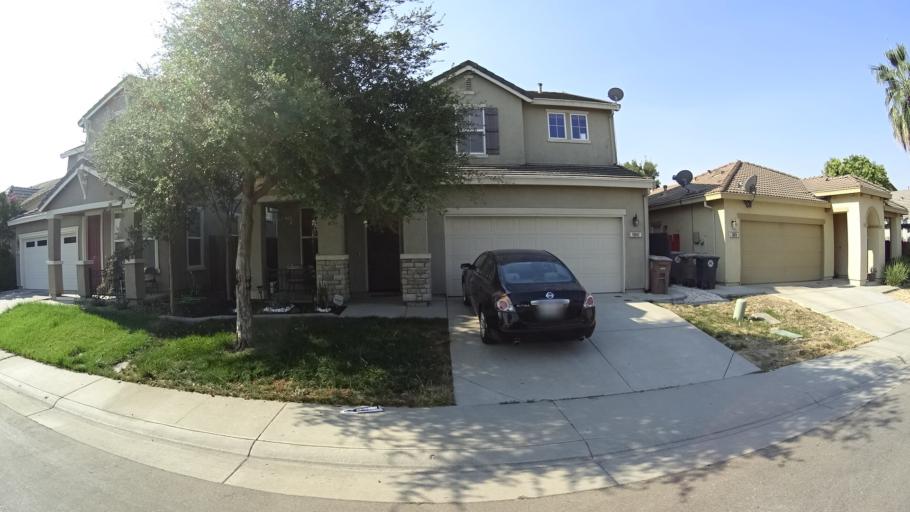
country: US
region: California
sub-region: Sacramento County
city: Laguna
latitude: 38.3908
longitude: -121.4372
